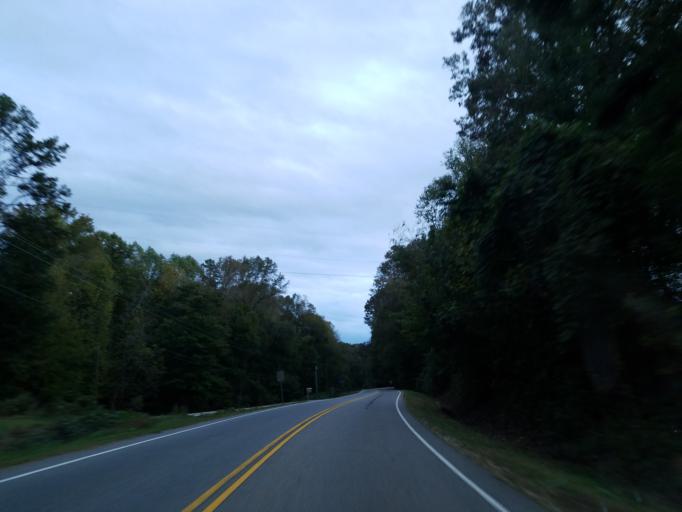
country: US
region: Georgia
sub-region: Dawson County
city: Dawsonville
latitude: 34.3850
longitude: -84.1247
